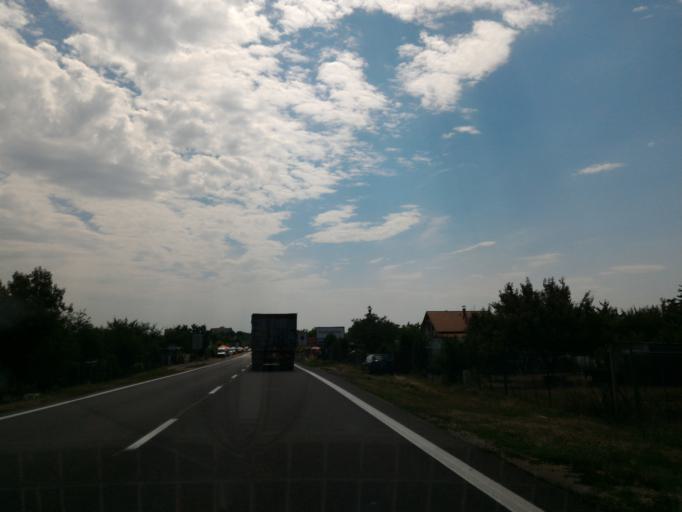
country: CZ
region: South Moravian
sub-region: Okres Znojmo
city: Znojmo
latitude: 48.8728
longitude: 16.0244
